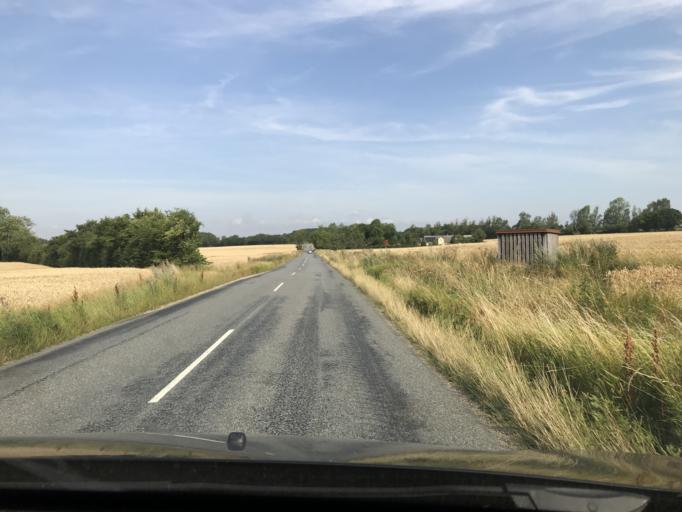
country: DK
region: Central Jutland
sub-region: Norddjurs Kommune
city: Allingabro
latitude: 56.5191
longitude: 10.3272
